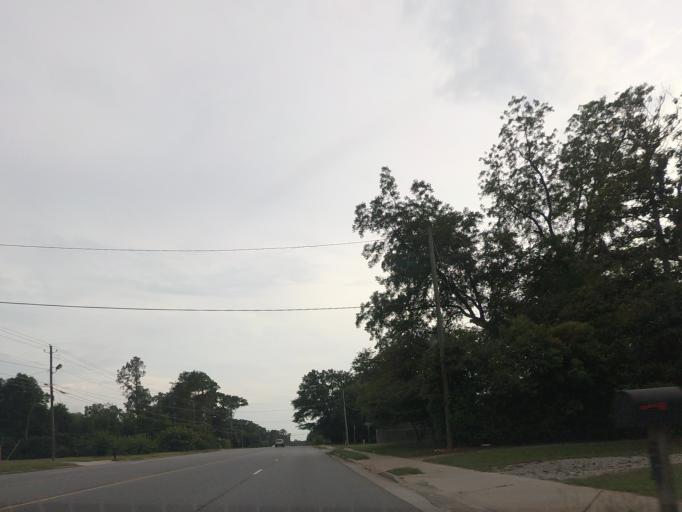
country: US
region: Georgia
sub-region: Houston County
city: Centerville
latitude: 32.7382
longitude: -83.6768
